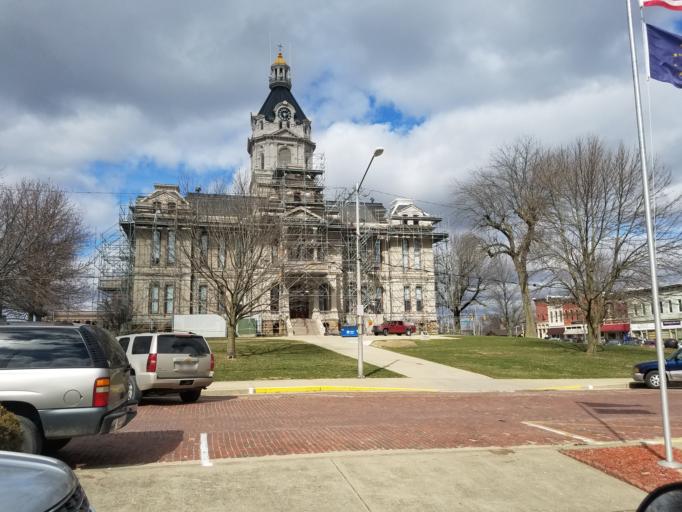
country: US
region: Indiana
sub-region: Parke County
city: Rockville
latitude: 39.7626
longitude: -87.2303
